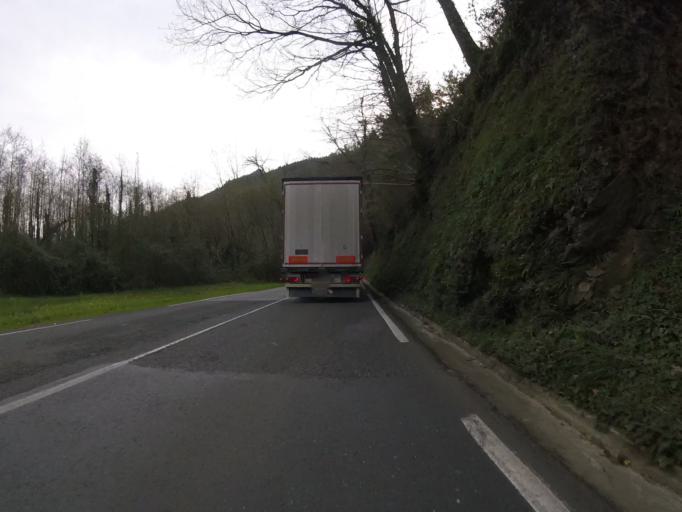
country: ES
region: Basque Country
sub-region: Provincia de Guipuzcoa
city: Cestona
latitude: 43.2534
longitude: -2.2542
